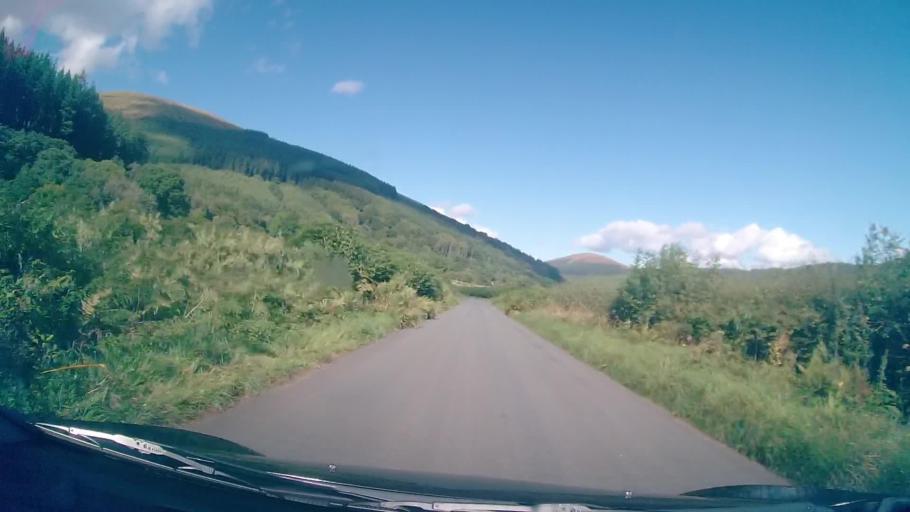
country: GB
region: Wales
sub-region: Caerphilly County Borough
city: Rhymney
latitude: 51.8459
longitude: -3.3387
